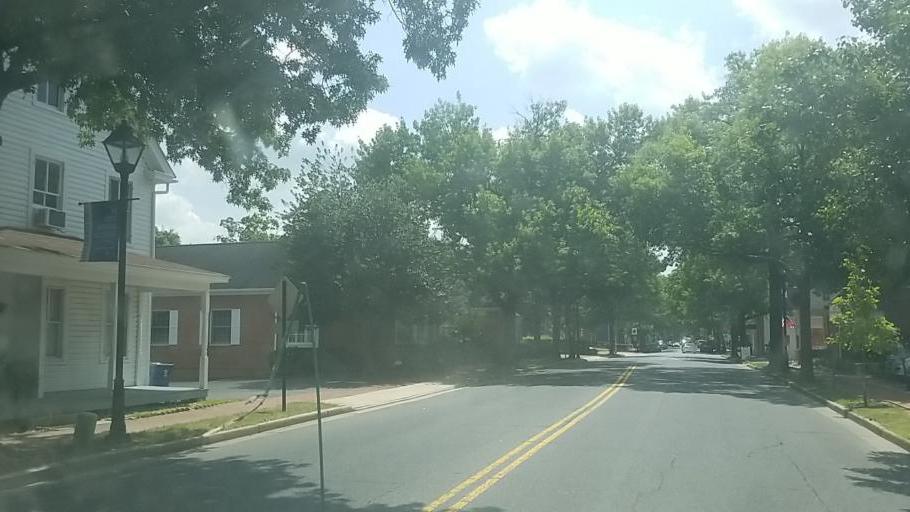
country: US
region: Maryland
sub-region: Talbot County
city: Easton
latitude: 38.7766
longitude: -76.0752
